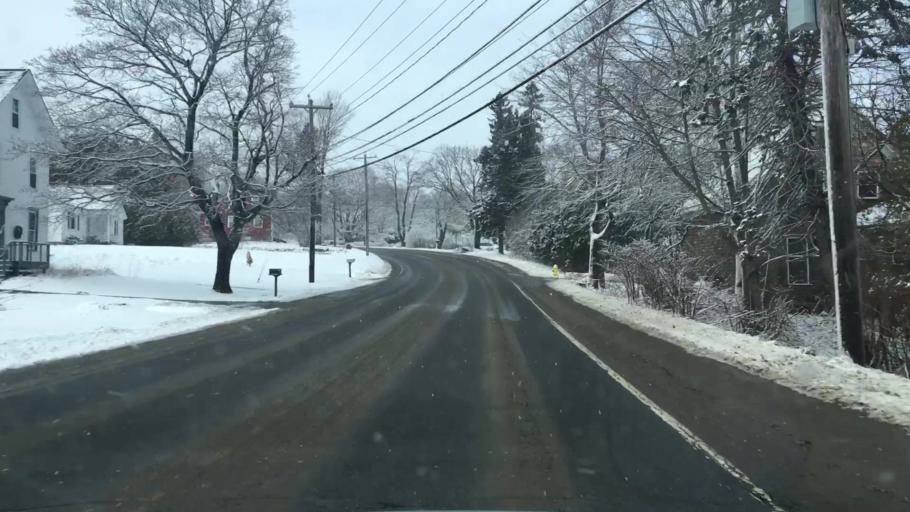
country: US
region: Maine
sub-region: Knox County
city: Rockland
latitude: 44.0848
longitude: -69.1060
